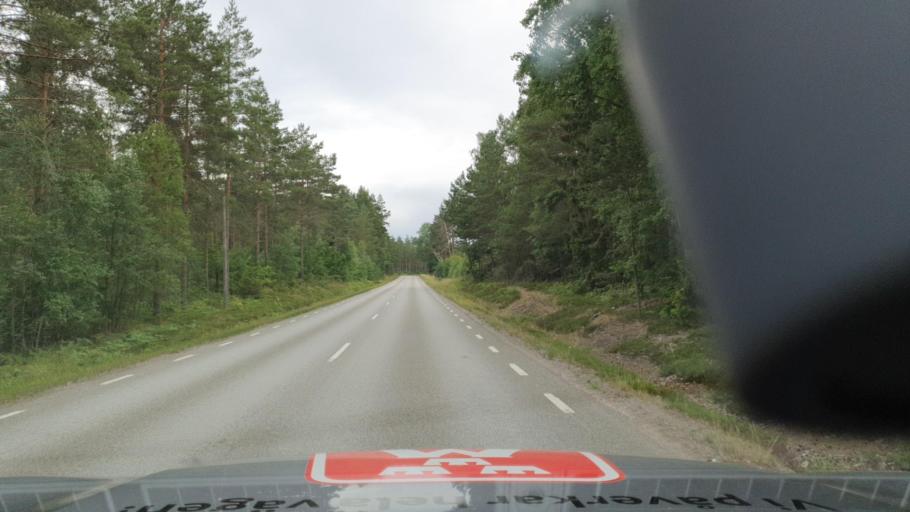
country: SE
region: Kalmar
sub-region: Nybro Kommun
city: Nybro
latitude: 56.6787
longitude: 15.9932
